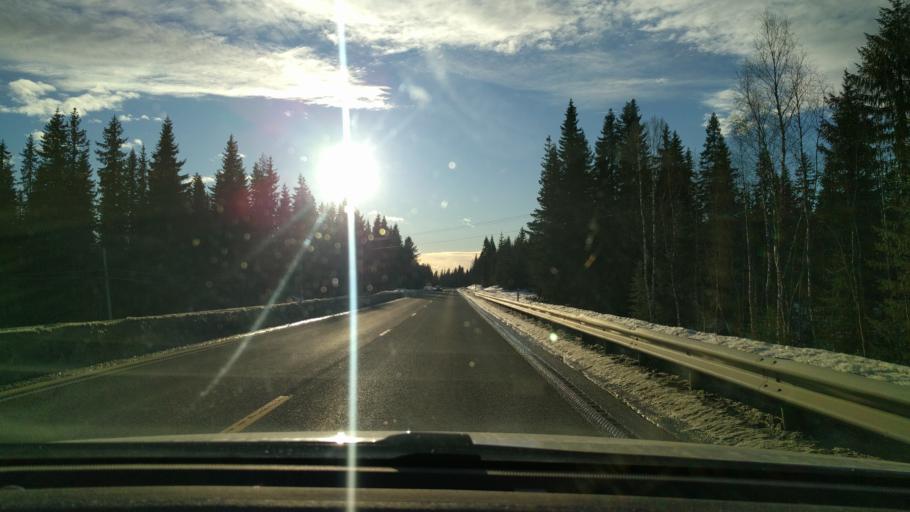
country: NO
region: Hedmark
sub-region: Valer
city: Valer
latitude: 61.0490
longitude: 11.9247
